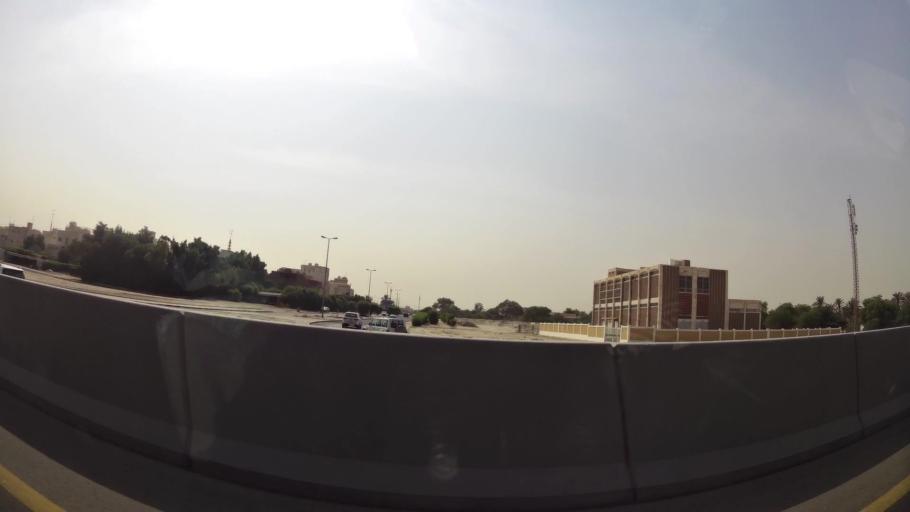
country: KW
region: Al Asimah
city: Ar Rabiyah
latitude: 29.3086
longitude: 47.8902
